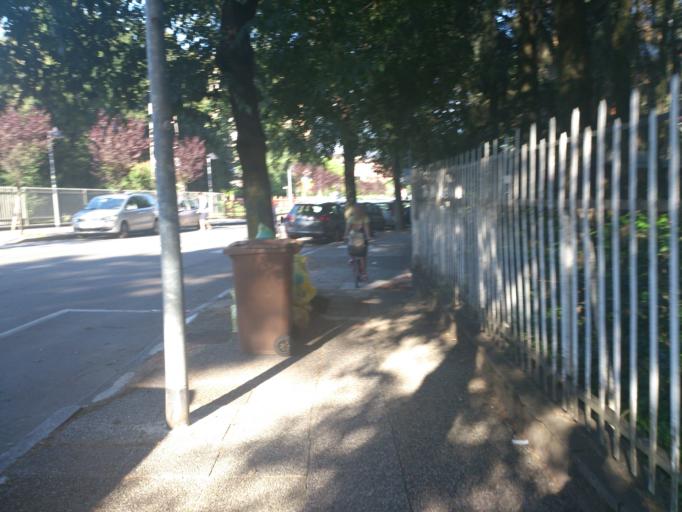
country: IT
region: Lombardy
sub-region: Citta metropolitana di Milano
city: San Donato Milanese
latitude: 45.4295
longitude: 9.2638
